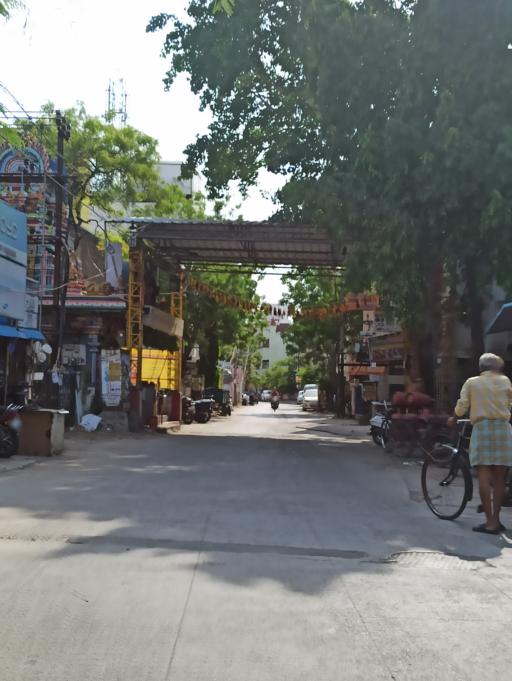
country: IN
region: Tamil Nadu
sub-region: Chennai
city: Chetput
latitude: 13.0587
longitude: 80.2180
